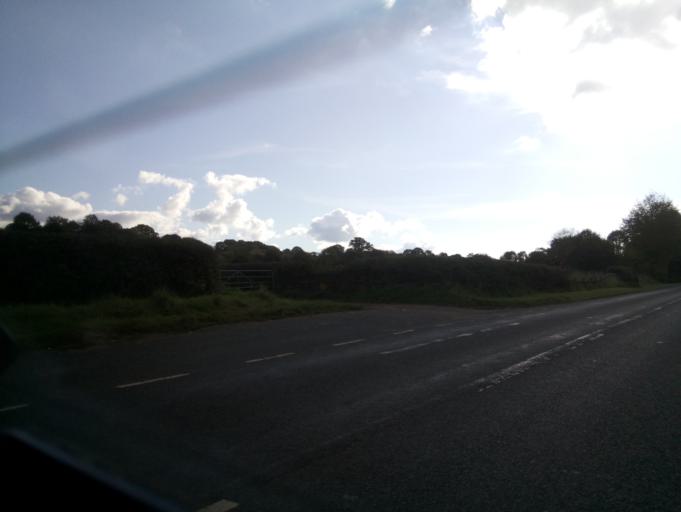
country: GB
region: Wales
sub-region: Sir Powys
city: Hay
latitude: 52.0572
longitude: -3.1668
